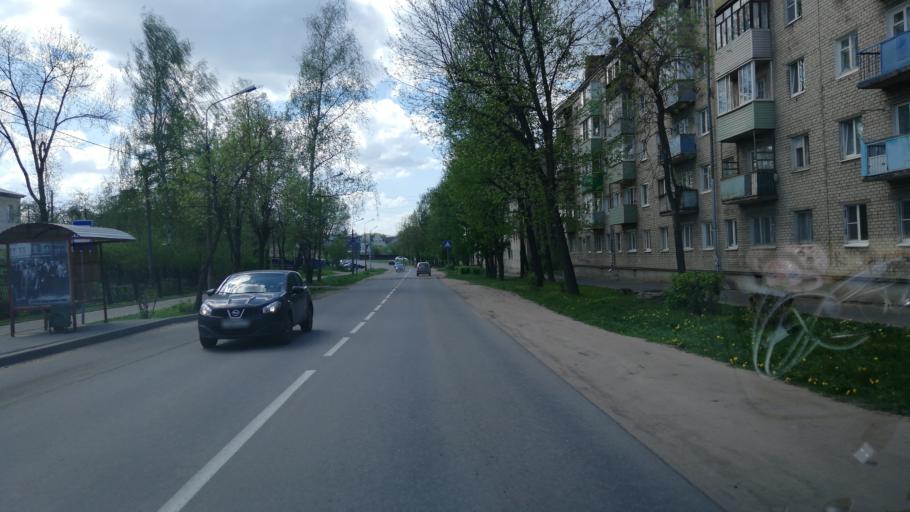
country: RU
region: Jaroslavl
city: Uglich
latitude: 57.5346
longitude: 38.3378
